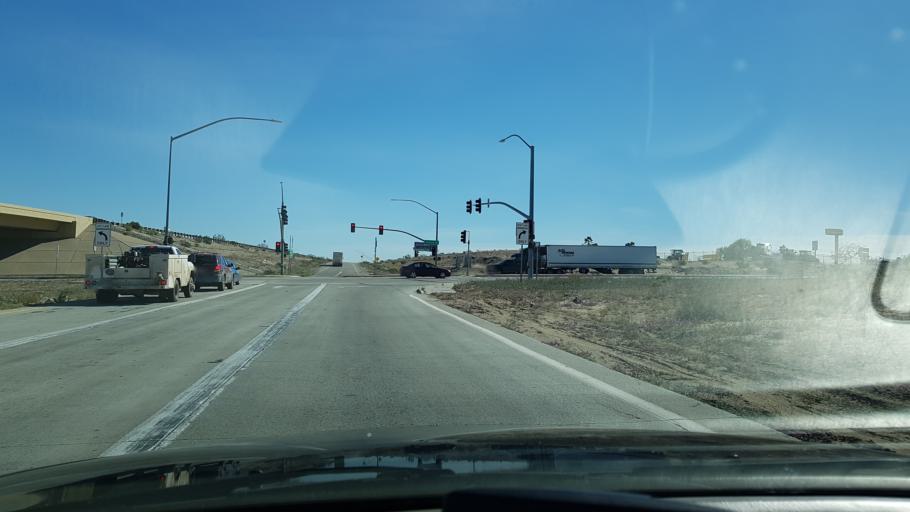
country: US
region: Arizona
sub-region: Yuma County
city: Yuma
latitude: 32.6887
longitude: -114.5825
